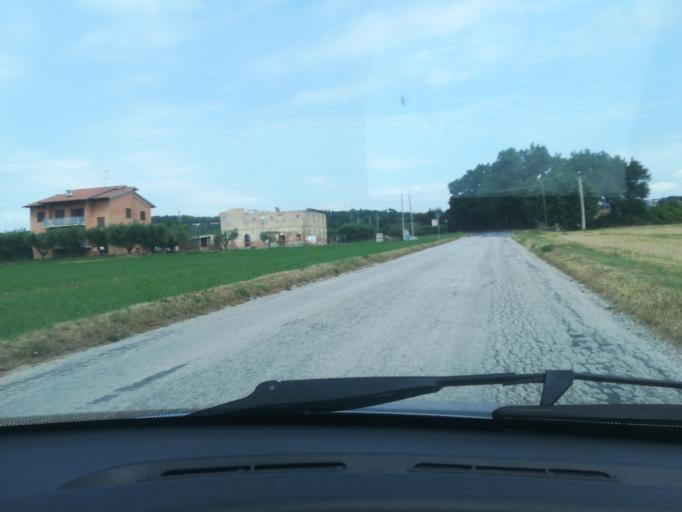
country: IT
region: The Marches
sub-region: Provincia di Macerata
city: Sforzacosta
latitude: 43.2679
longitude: 13.4384
